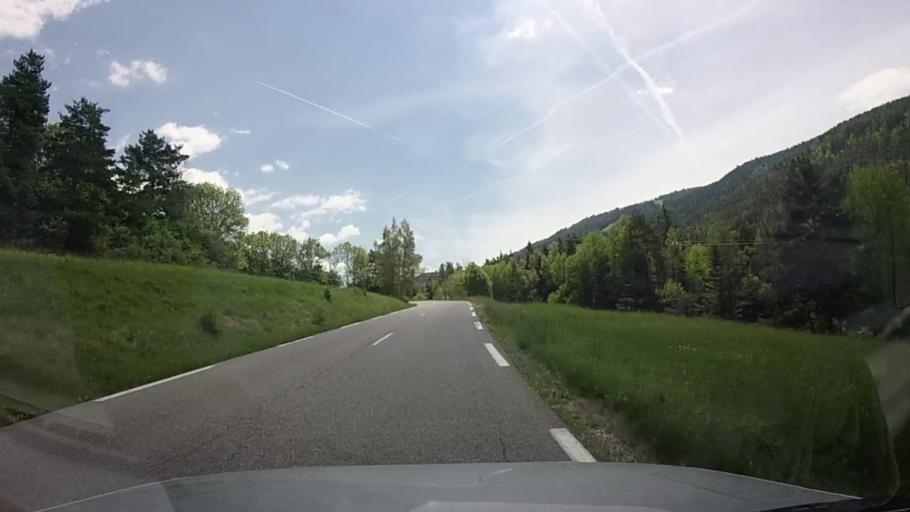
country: FR
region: Provence-Alpes-Cote d'Azur
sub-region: Departement des Alpes-de-Haute-Provence
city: Seyne-les-Alpes
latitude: 44.3360
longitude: 6.3863
